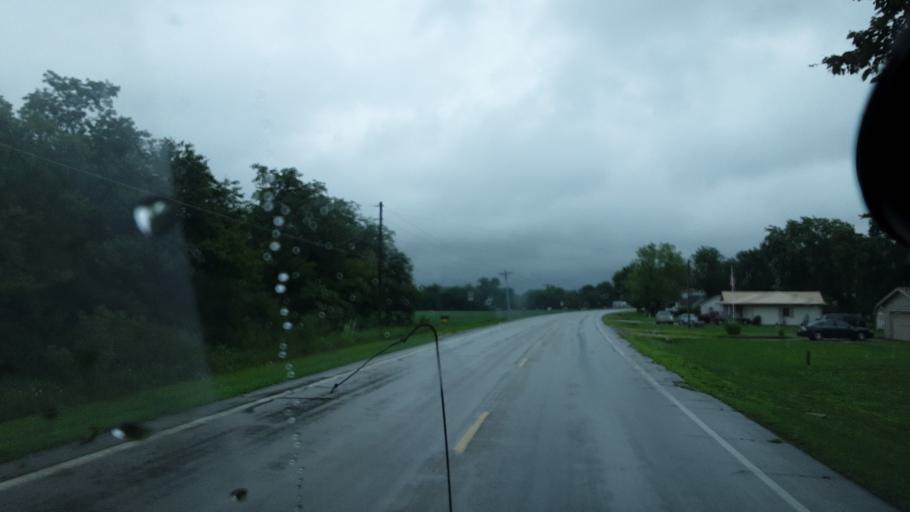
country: US
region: Indiana
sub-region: Adams County
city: Decatur
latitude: 40.7756
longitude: -84.8378
